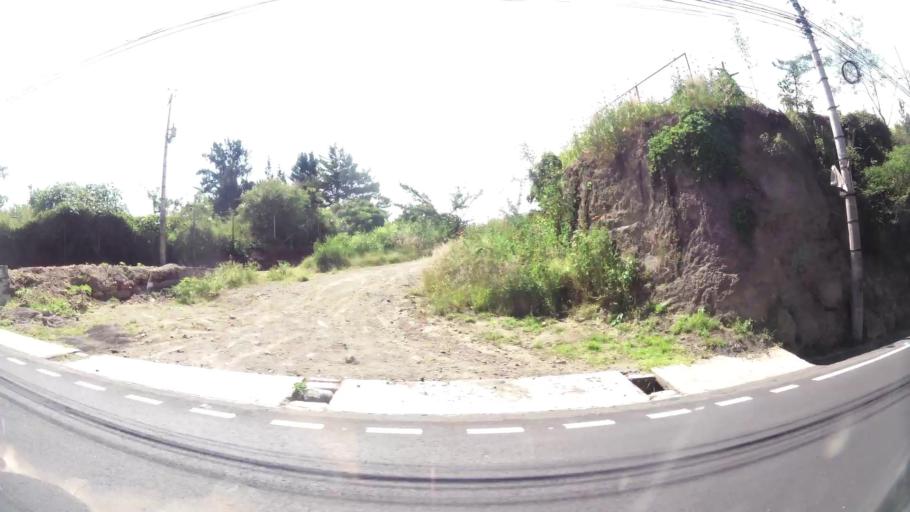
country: EC
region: Pichincha
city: Quito
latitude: -0.2107
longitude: -78.4244
